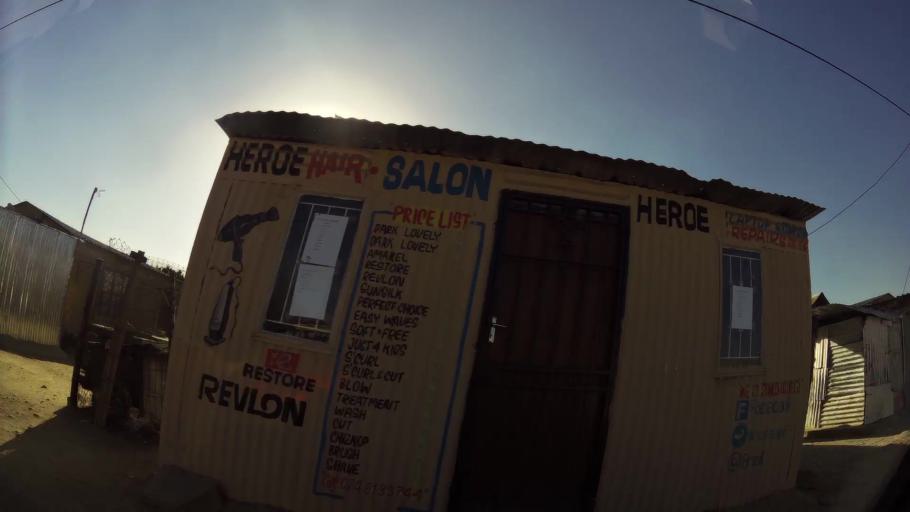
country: ZA
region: Gauteng
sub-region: City of Johannesburg Metropolitan Municipality
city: Diepsloot
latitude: -25.9280
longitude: 28.0011
